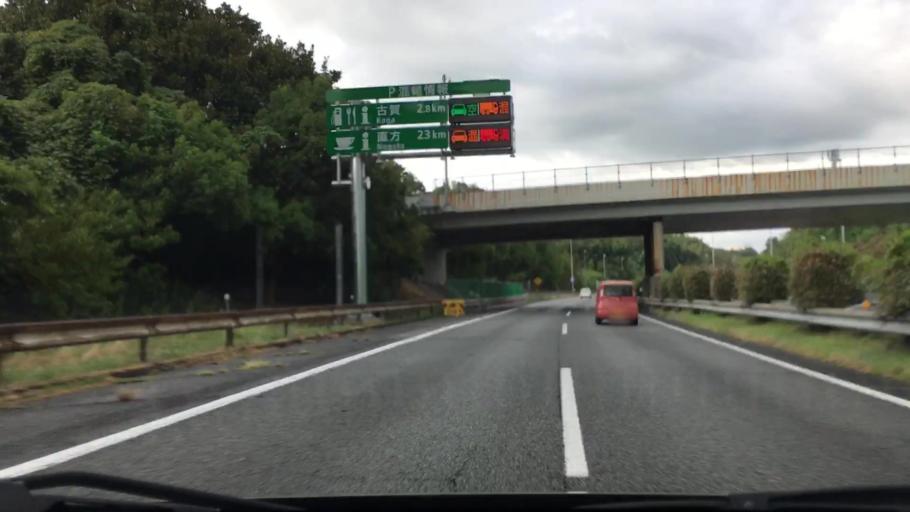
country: JP
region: Fukuoka
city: Koga
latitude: 33.7183
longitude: 130.4928
